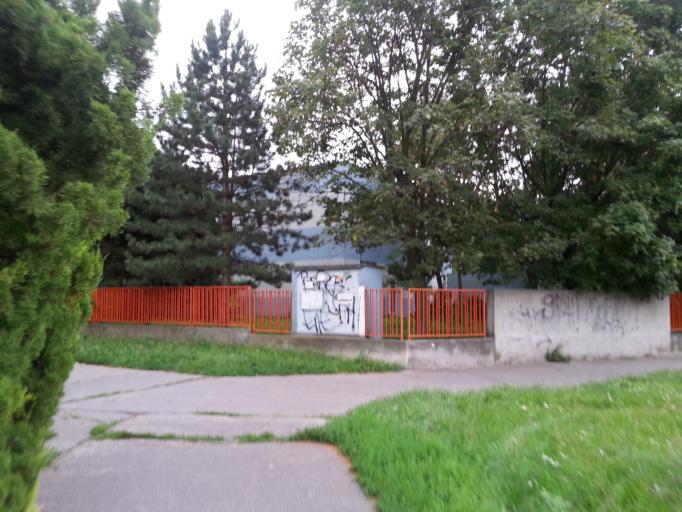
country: SK
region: Bratislavsky
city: Bratislava
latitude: 48.1287
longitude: 17.1018
